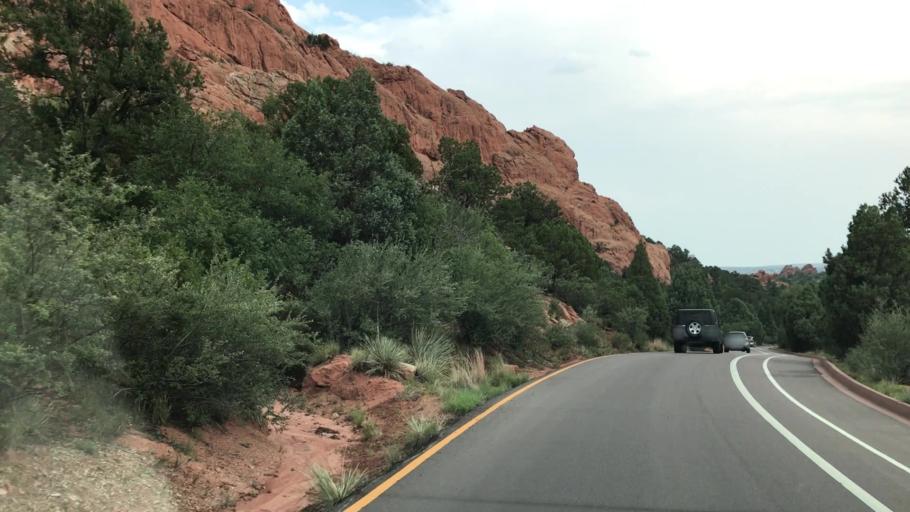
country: US
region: Colorado
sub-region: El Paso County
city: Manitou Springs
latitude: 38.8740
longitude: -104.8824
